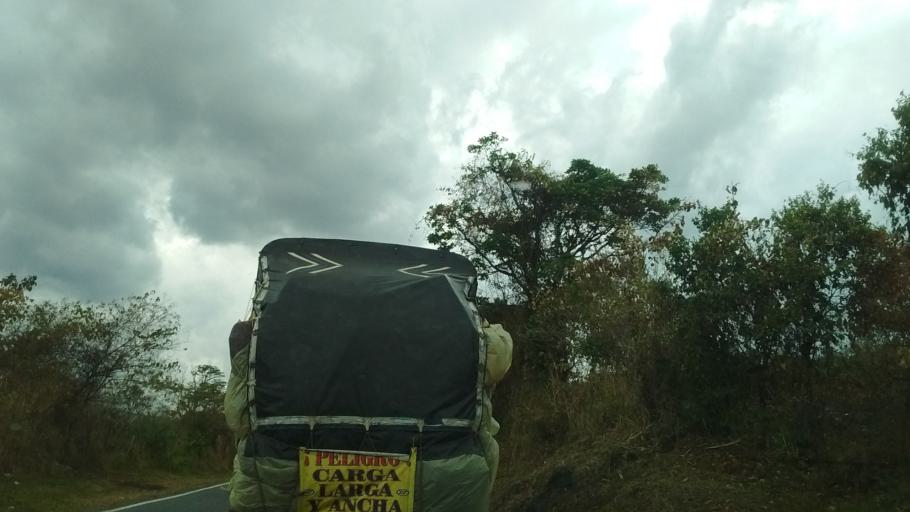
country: CO
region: Cauca
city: Rosas
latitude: 2.2790
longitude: -76.7259
